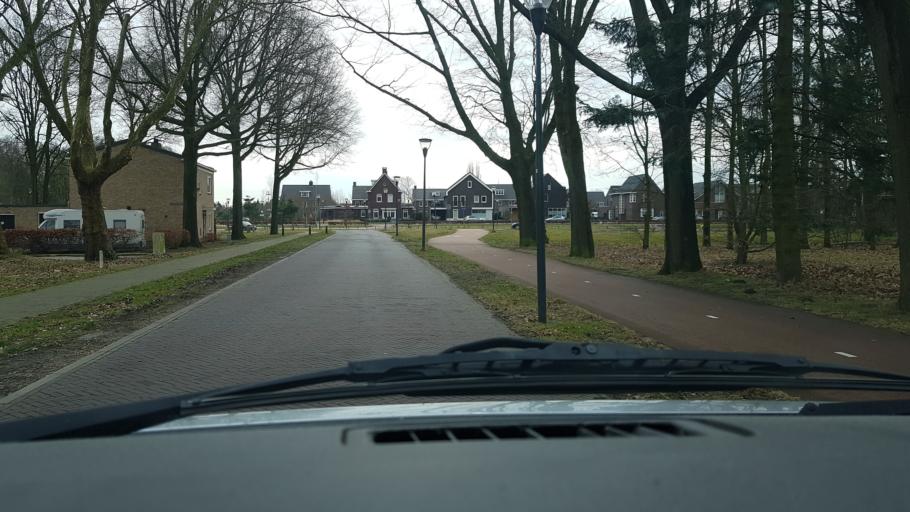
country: NL
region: North Brabant
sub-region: Gemeente Eindhoven
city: Meerhoven
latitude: 51.4440
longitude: 5.4180
